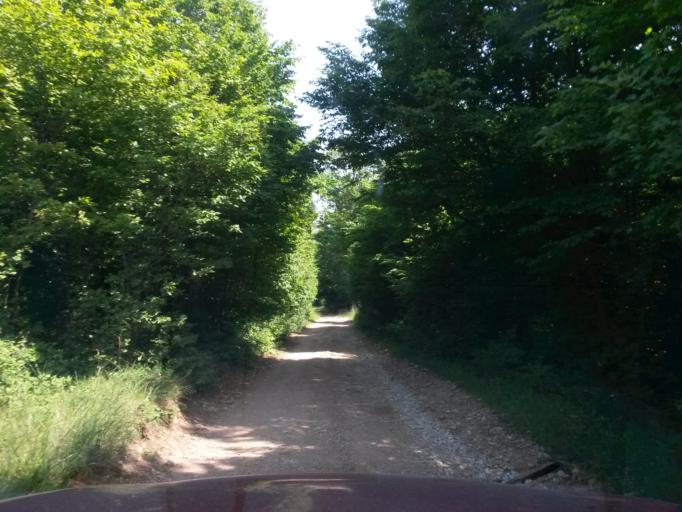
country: SK
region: Kosicky
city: Moldava nad Bodvou
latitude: 48.6439
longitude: 20.9530
